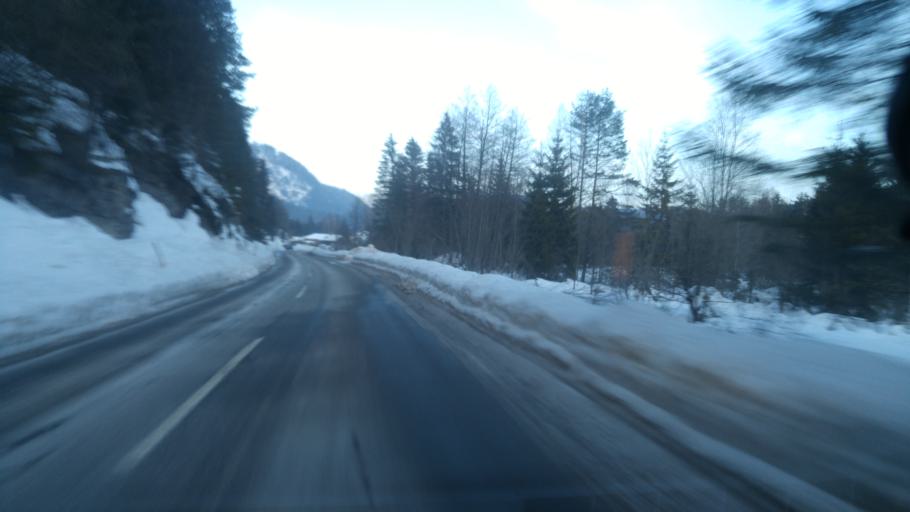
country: AT
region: Lower Austria
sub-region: Politischer Bezirk Wiener Neustadt
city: Rohr im Gebirge
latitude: 47.8849
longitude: 15.7129
